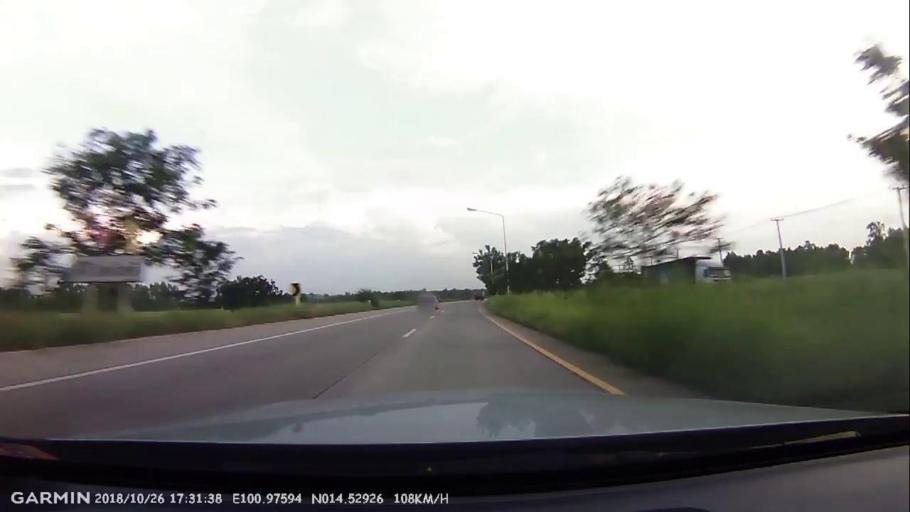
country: TH
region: Sara Buri
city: Saraburi
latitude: 14.5288
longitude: 100.9762
